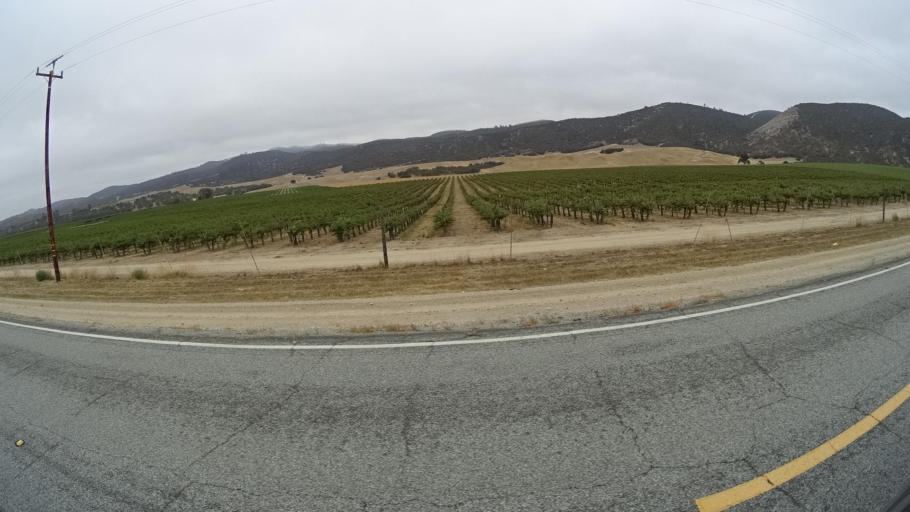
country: US
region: California
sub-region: San Luis Obispo County
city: Lake Nacimiento
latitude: 35.8826
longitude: -120.9045
